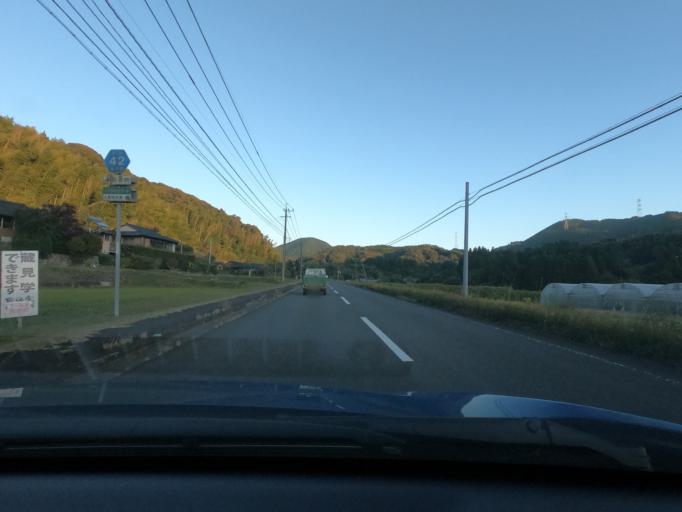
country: JP
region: Kagoshima
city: Satsumasendai
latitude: 31.7904
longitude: 130.4638
